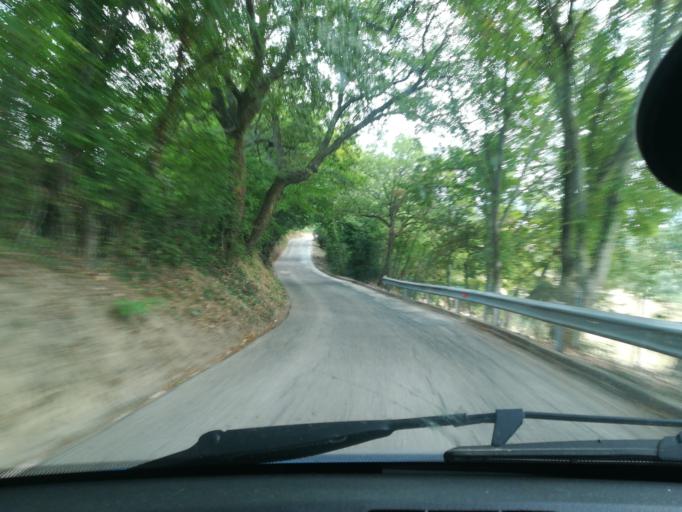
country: IT
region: The Marches
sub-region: Provincia di Macerata
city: Piediripa
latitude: 43.2945
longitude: 13.4851
